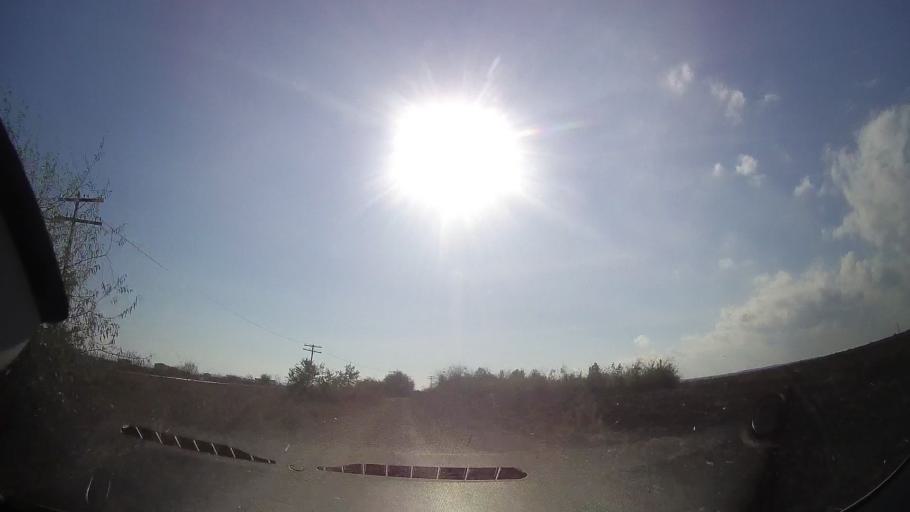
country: RO
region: Constanta
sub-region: Comuna Costinesti
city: Costinesti
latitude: 43.9744
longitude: 28.6439
